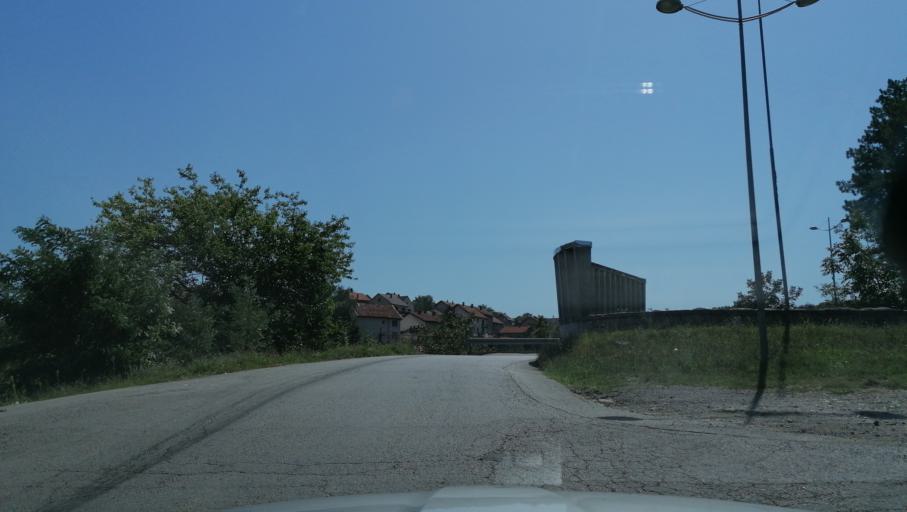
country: RS
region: Central Serbia
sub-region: Kolubarski Okrug
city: Valjevo
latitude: 44.2649
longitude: 19.8817
